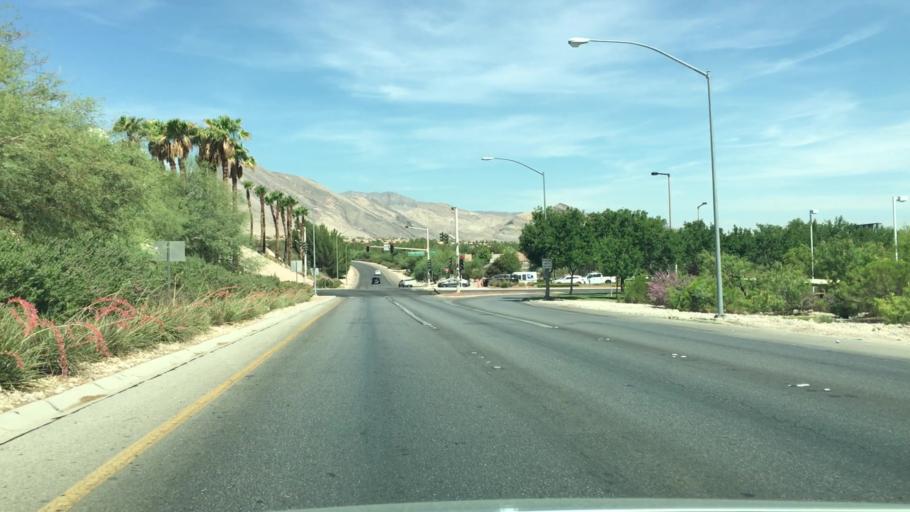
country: US
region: Nevada
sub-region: Clark County
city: Summerlin South
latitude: 36.1865
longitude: -115.3054
